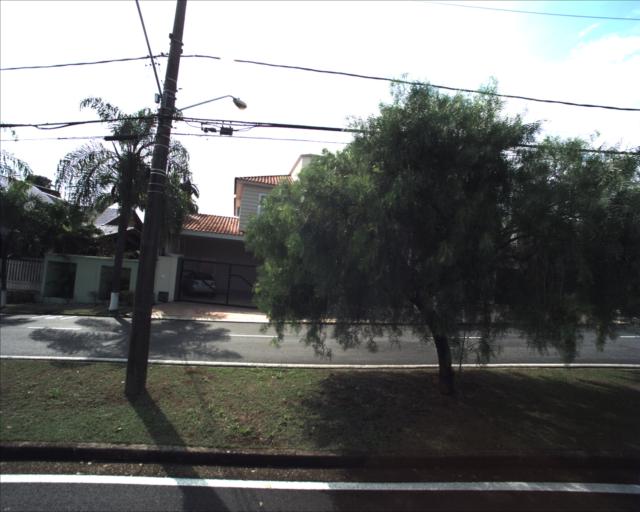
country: BR
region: Sao Paulo
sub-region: Sorocaba
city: Sorocaba
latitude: -23.5206
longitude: -47.4709
